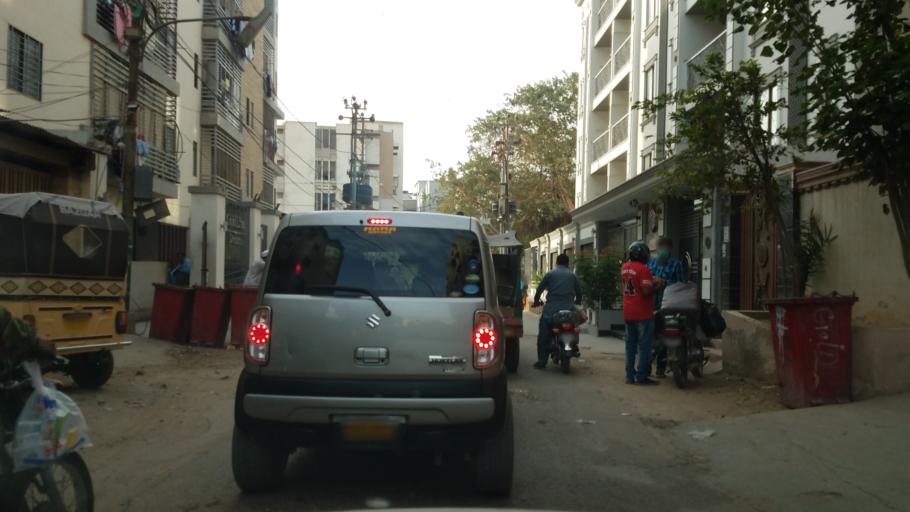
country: PK
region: Sindh
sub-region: Karachi District
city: Karachi
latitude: 24.8794
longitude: 67.0380
